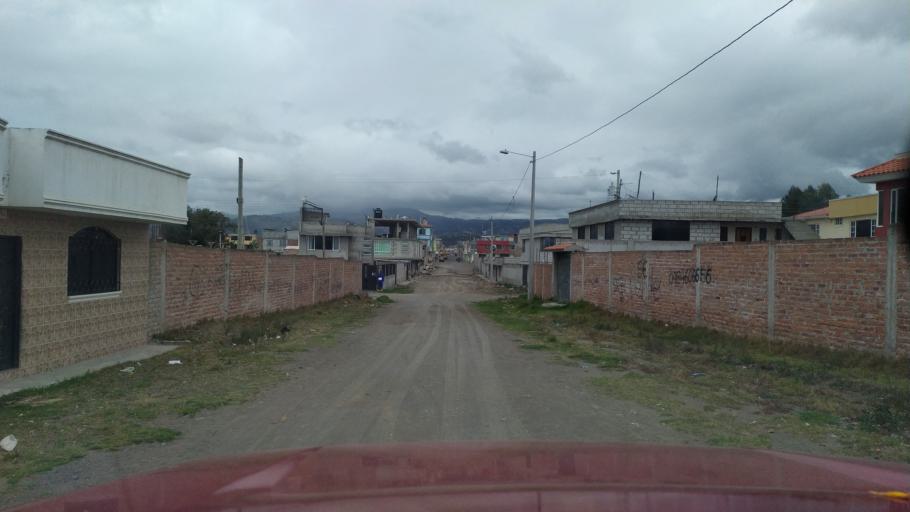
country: EC
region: Chimborazo
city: Riobamba
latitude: -1.6587
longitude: -78.6364
